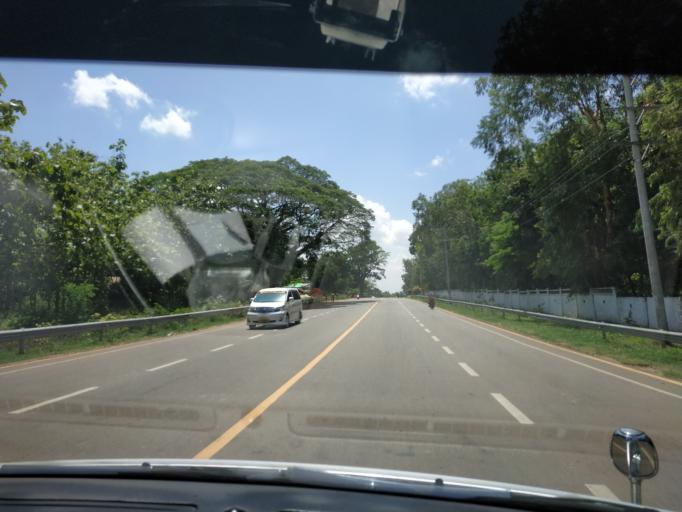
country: MM
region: Mon
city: Kyaikto
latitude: 17.3125
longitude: 97.0232
